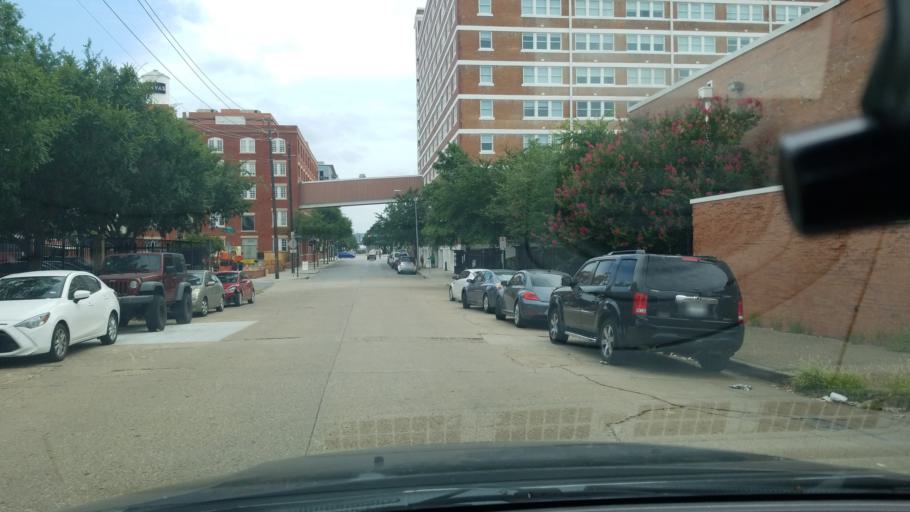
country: US
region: Texas
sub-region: Dallas County
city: Dallas
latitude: 32.7666
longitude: -96.7969
